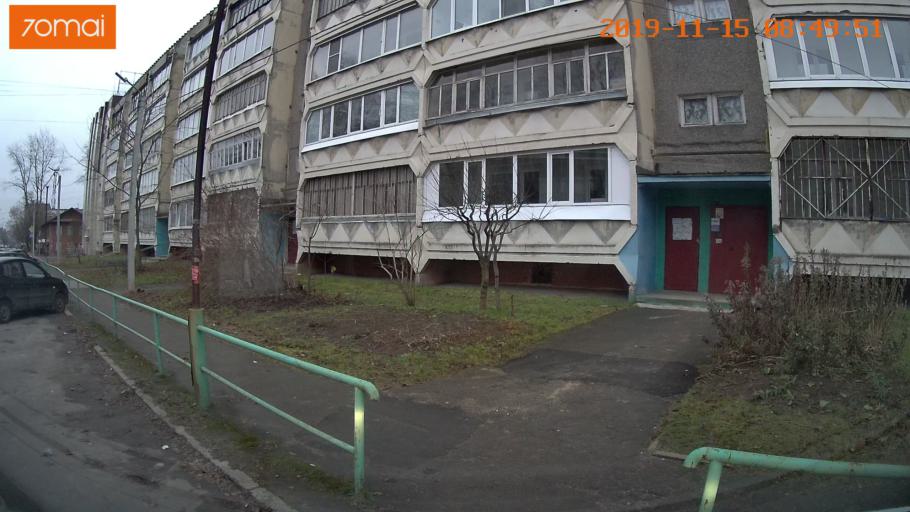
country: RU
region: Vologda
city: Cherepovets
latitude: 59.1236
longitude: 37.9230
